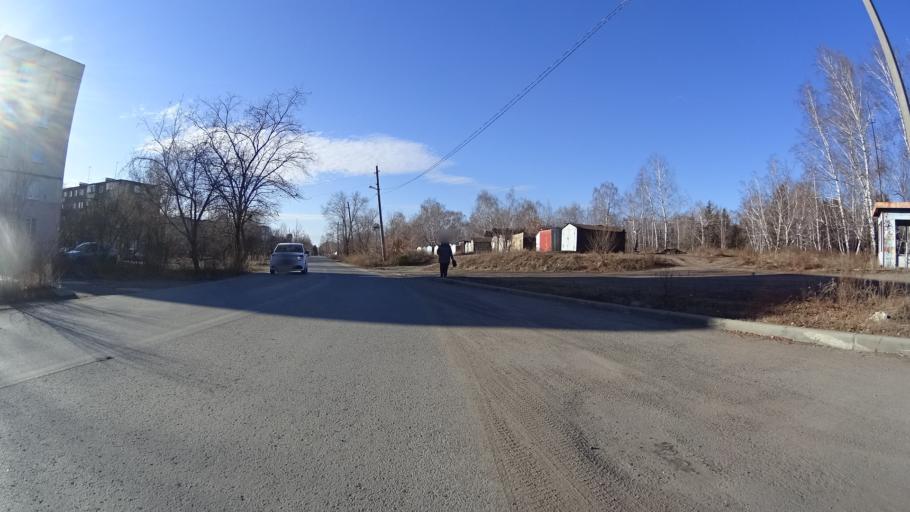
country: RU
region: Chelyabinsk
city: Troitsk
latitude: 54.0532
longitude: 61.6396
